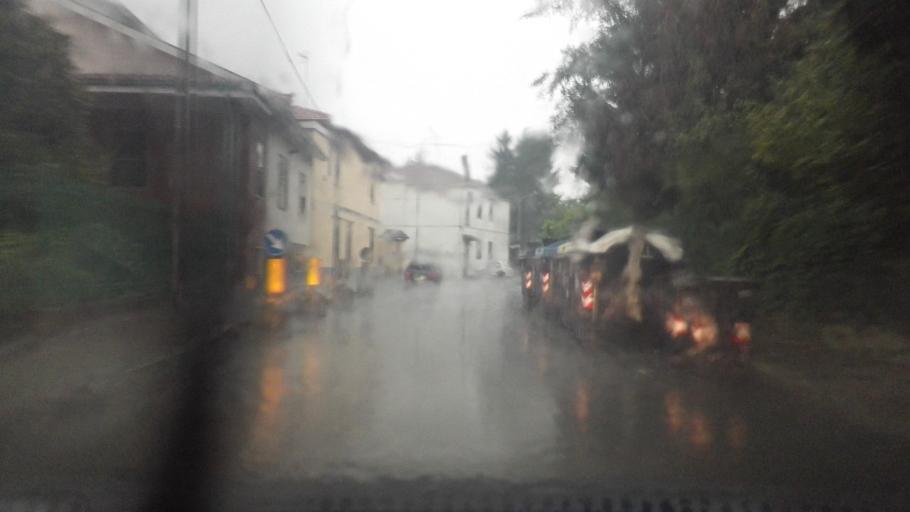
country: IT
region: Piedmont
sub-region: Provincia di Alessandria
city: Alessandria
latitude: 44.9292
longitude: 8.6204
